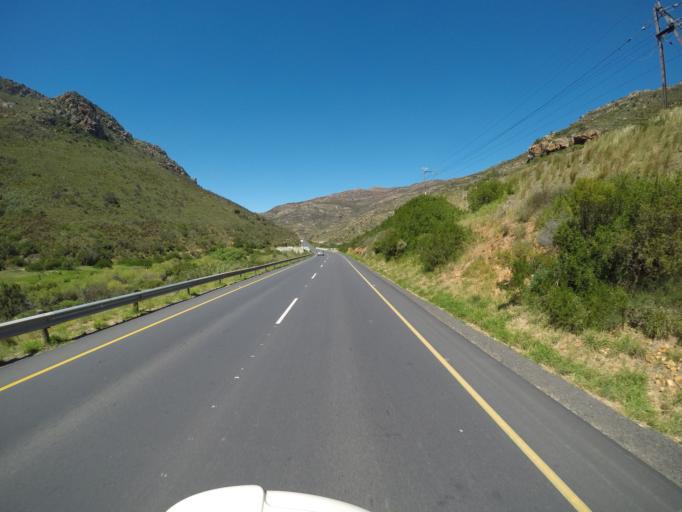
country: ZA
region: Western Cape
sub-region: Cape Winelands District Municipality
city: Ceres
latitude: -33.3113
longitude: 19.0727
